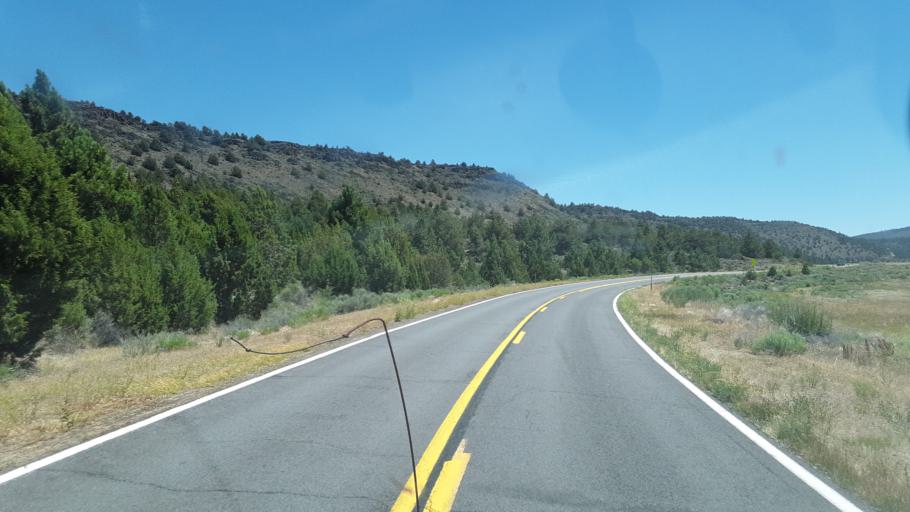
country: US
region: California
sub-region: Lassen County
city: Susanville
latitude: 40.6833
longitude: -120.6611
